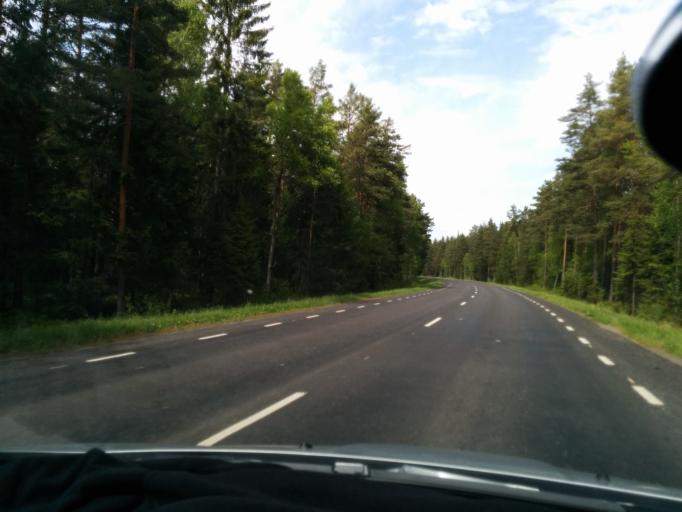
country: EE
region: Harju
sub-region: Loksa linn
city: Loksa
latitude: 59.5439
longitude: 25.7377
